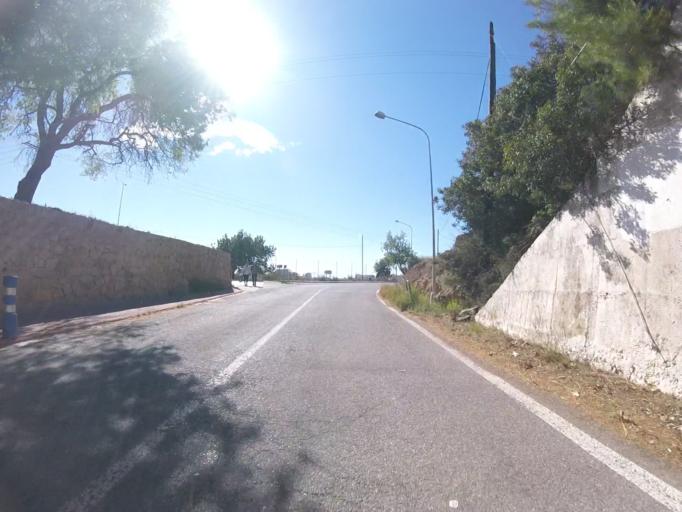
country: ES
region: Valencia
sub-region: Provincia de Castello
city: Benicassim
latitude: 40.0596
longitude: 0.0683
